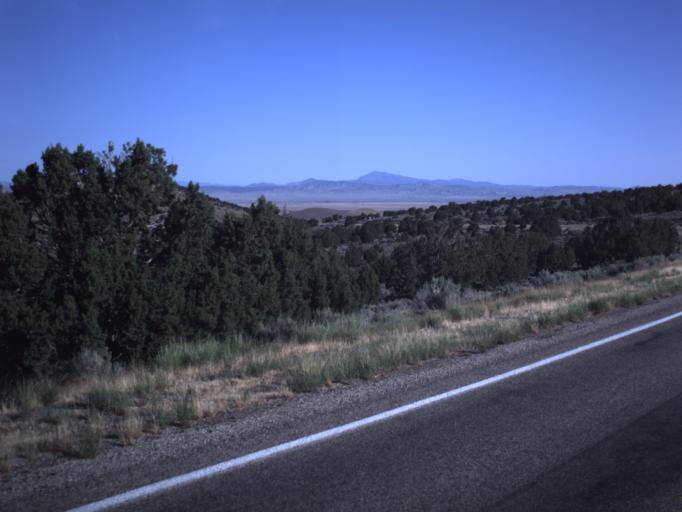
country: US
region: Utah
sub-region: Beaver County
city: Milford
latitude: 38.1210
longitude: -112.9510
